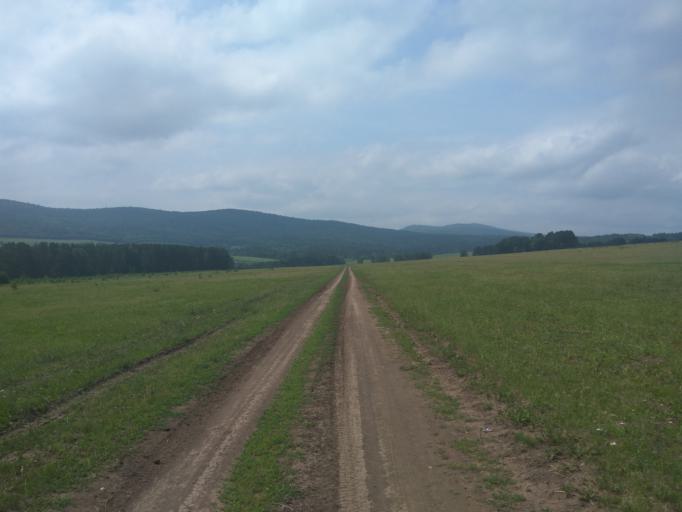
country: RU
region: Krasnoyarskiy
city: Zykovo
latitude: 55.8472
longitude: 93.2107
